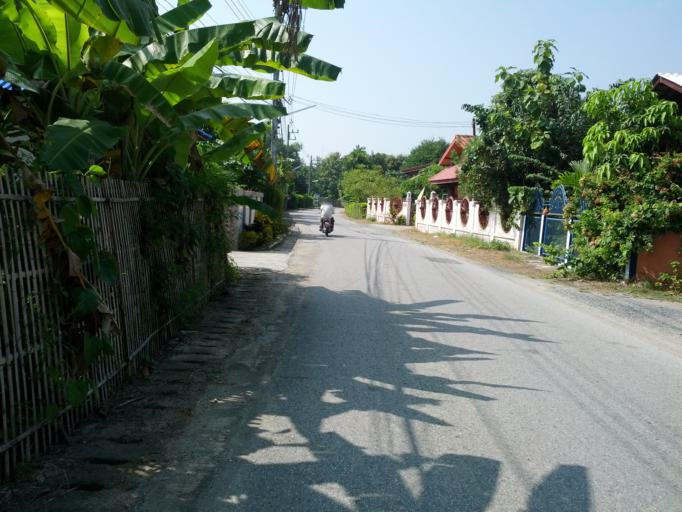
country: TH
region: Chiang Mai
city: San Sai
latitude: 18.8037
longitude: 99.0910
